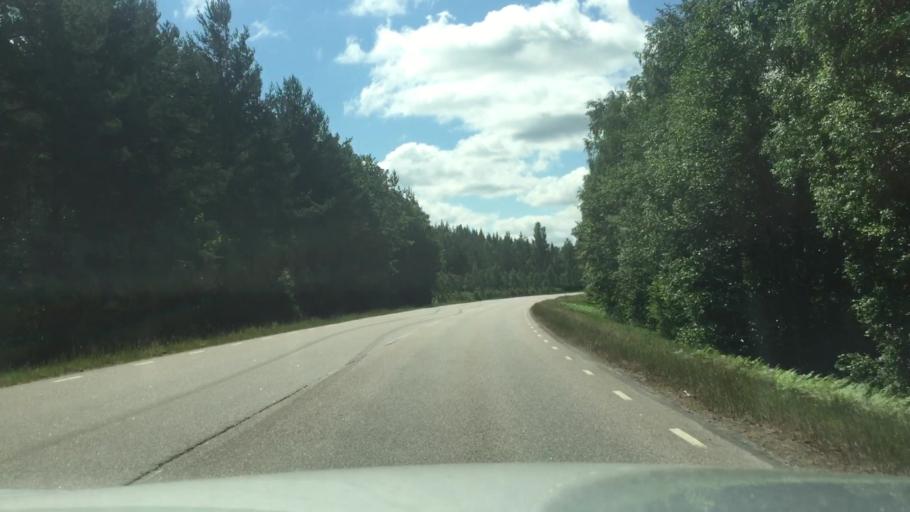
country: SE
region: Vaestra Goetaland
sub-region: Karlsborgs Kommun
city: Molltorp
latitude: 58.6165
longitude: 14.3896
